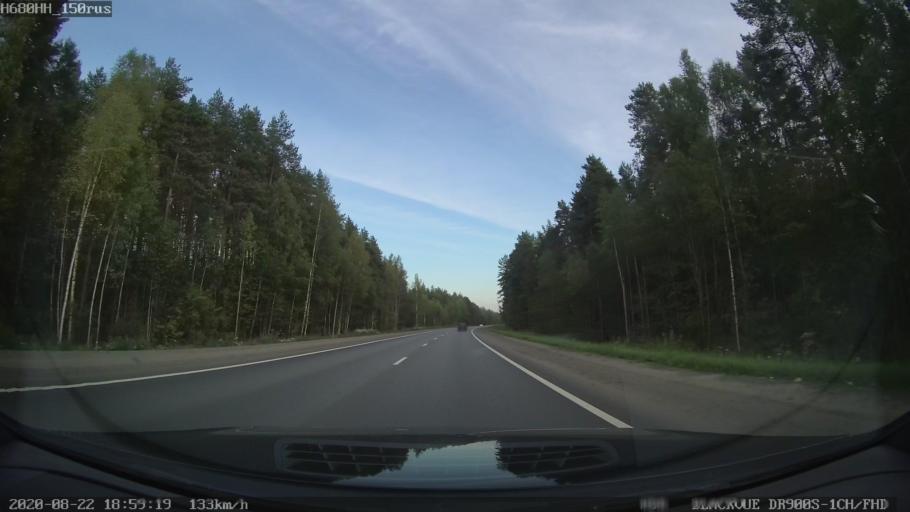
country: RU
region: Tverskaya
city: Rameshki
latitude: 57.1447
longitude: 36.0945
